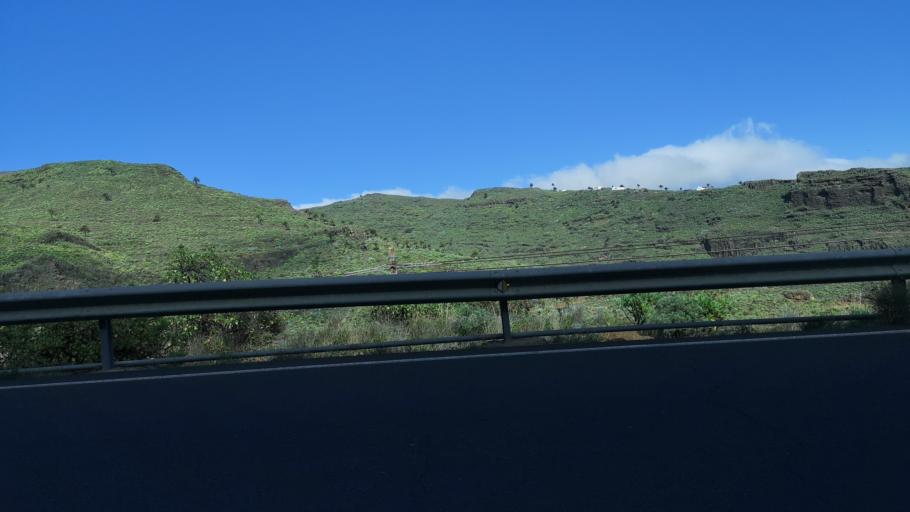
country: ES
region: Canary Islands
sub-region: Provincia de Santa Cruz de Tenerife
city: Alajero
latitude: 28.0648
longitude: -17.2033
